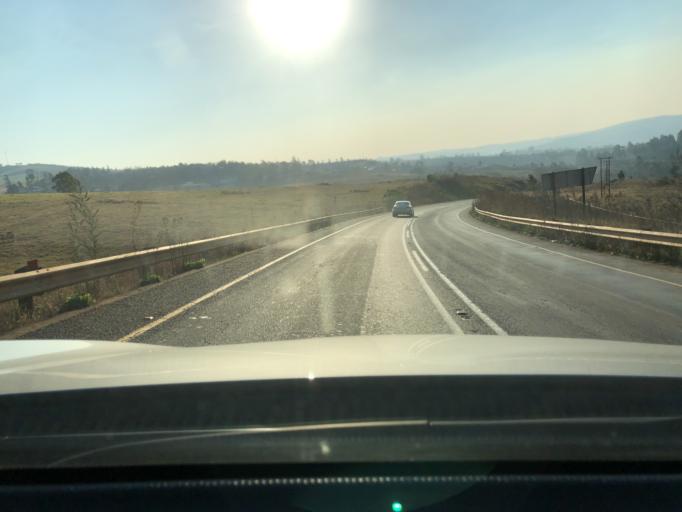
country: ZA
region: KwaZulu-Natal
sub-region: Sisonke District Municipality
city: Ixopo
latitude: -30.1630
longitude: 30.0874
